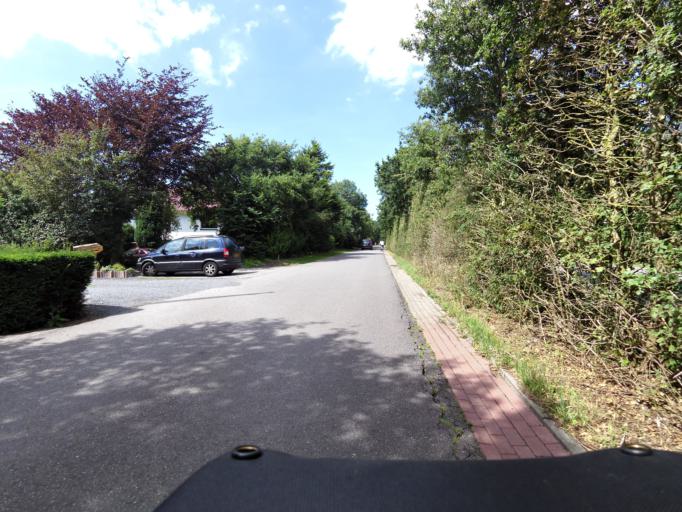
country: NL
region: South Holland
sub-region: Gemeente Goeree-Overflakkee
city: Ouddorp
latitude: 51.8244
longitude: 3.9347
